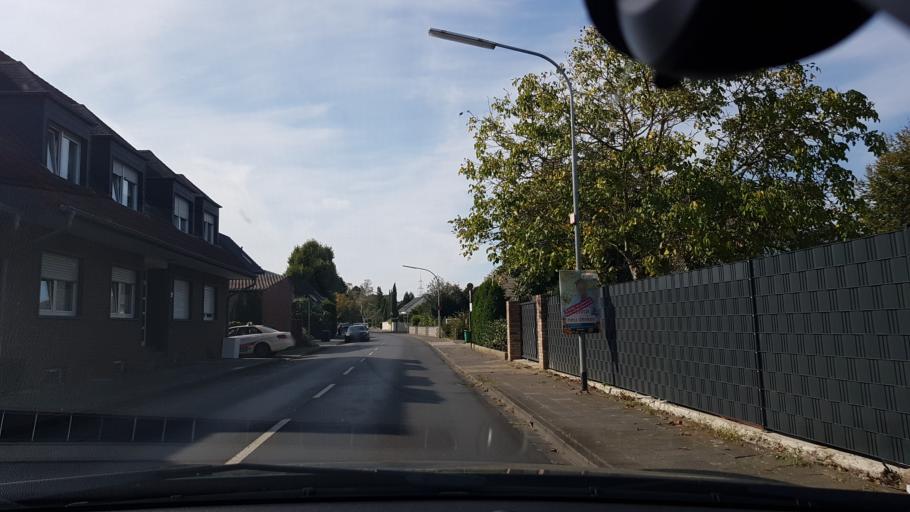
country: DE
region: North Rhine-Westphalia
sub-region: Regierungsbezirk Dusseldorf
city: Neuss
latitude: 51.1424
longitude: 6.7024
